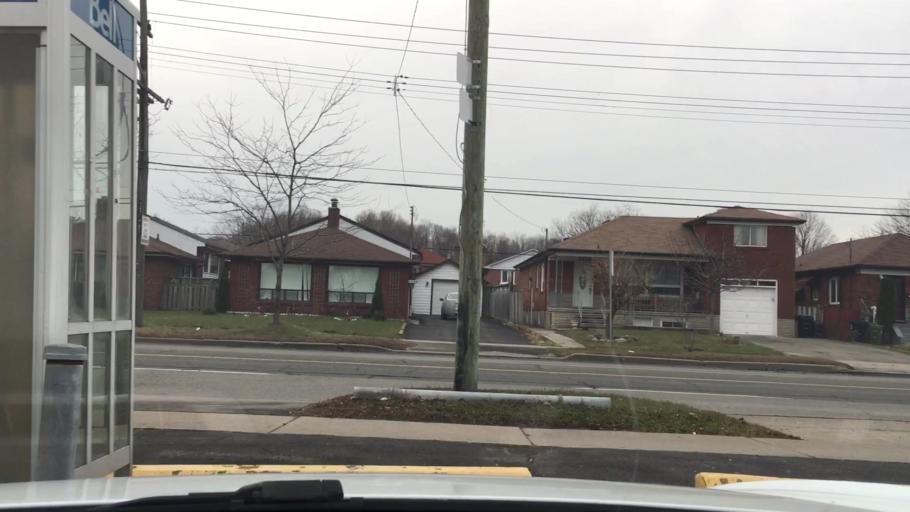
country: CA
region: Ontario
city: Scarborough
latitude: 43.7423
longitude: -79.2611
